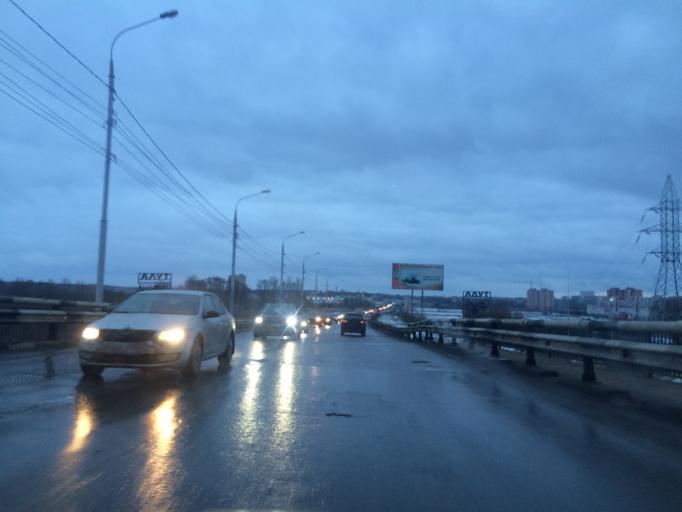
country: RU
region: Tula
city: Tula
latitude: 54.1918
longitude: 37.6577
